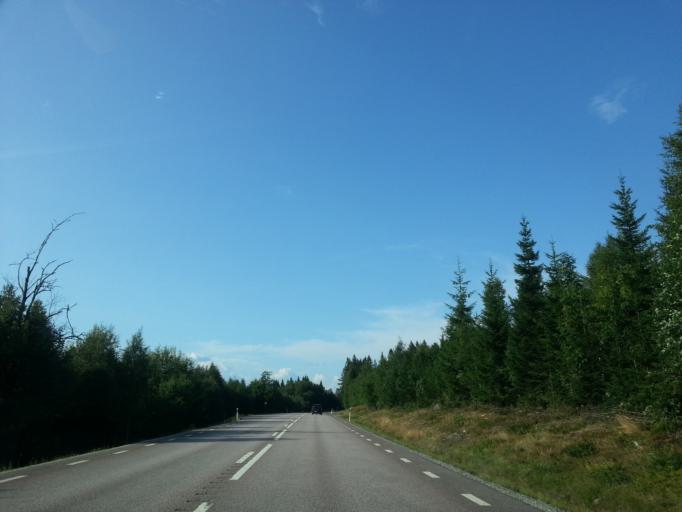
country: SE
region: Vaestmanland
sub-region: Skinnskattebergs Kommun
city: Skinnskatteberg
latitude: 59.9186
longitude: 15.7152
